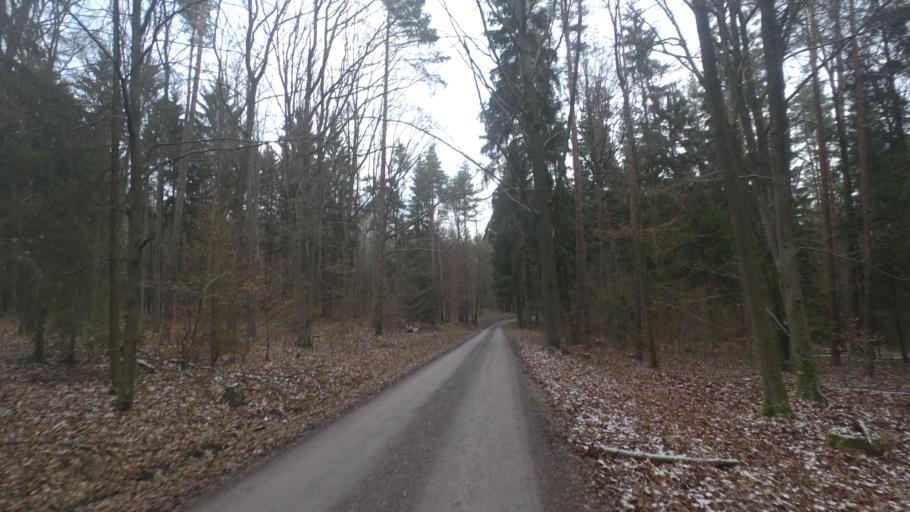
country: DE
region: Thuringia
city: Konitz
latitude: 50.6920
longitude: 11.4618
